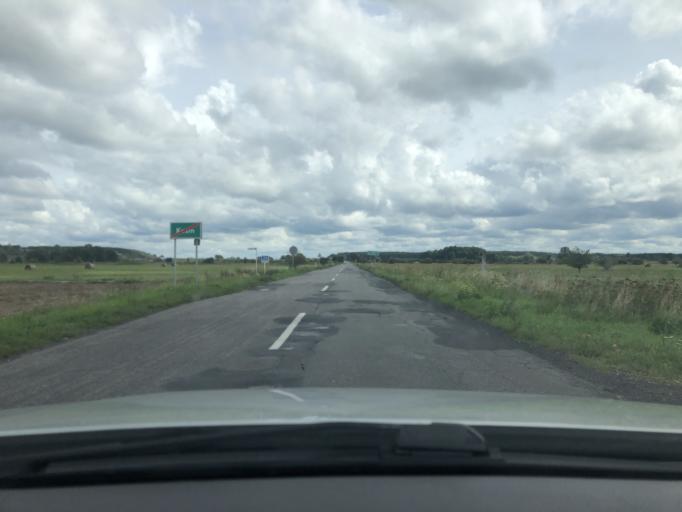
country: PL
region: Lubusz
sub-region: Powiat strzelecko-drezdenecki
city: Drezdenko
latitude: 52.8421
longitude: 15.9043
